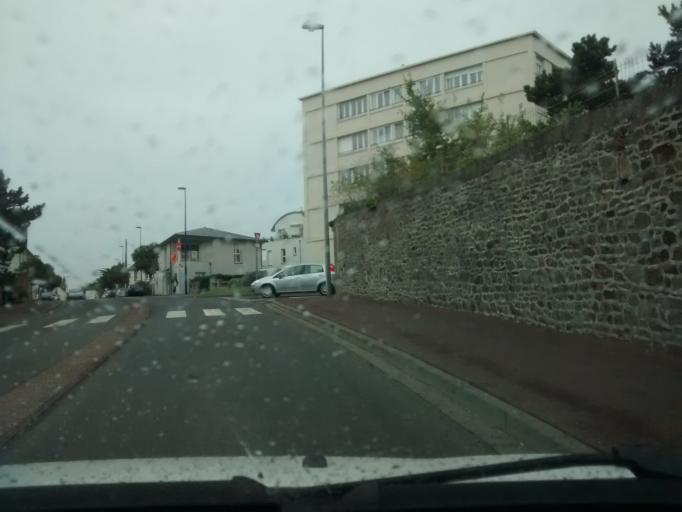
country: FR
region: Lower Normandy
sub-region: Departement de la Manche
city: Granville
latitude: 48.8328
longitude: -1.5852
